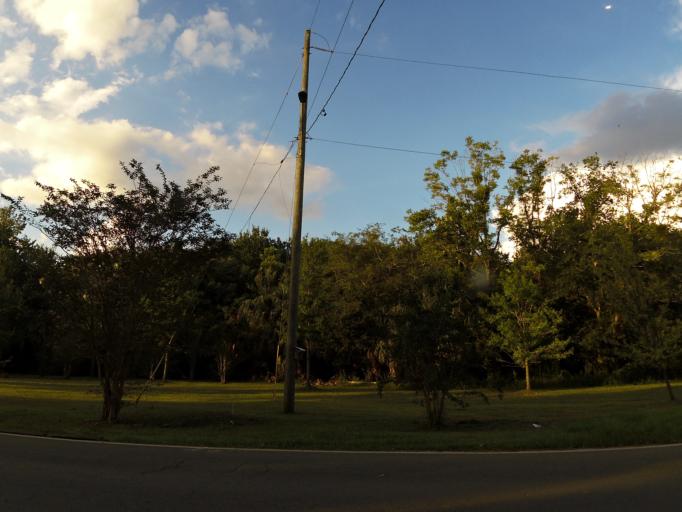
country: US
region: Florida
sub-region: Duval County
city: Jacksonville
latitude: 30.3272
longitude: -81.6835
